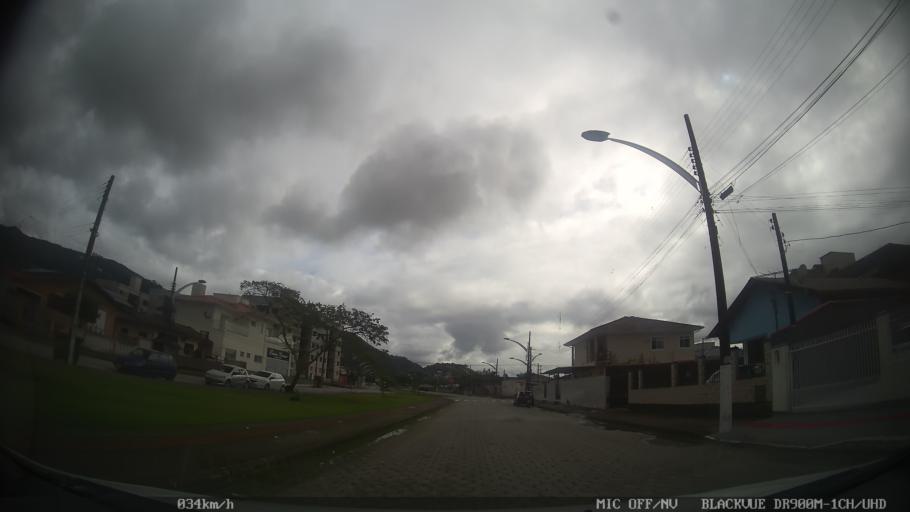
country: BR
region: Santa Catarina
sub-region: Biguacu
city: Biguacu
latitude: -27.5090
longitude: -48.6555
